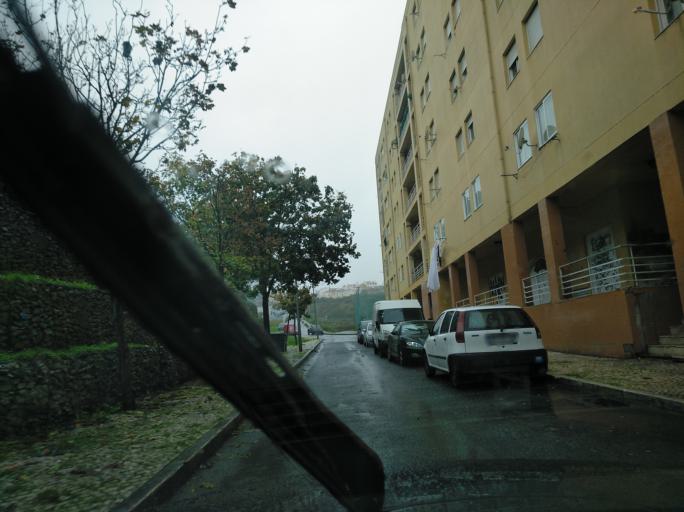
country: PT
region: Lisbon
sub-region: Lisbon
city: Lisbon
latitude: 38.7322
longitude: -9.1216
